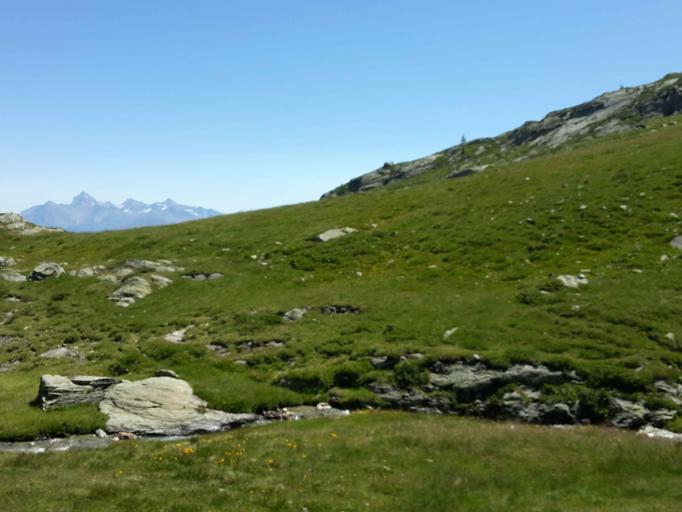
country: IT
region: Aosta Valley
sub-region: Valle d'Aosta
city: Valgrisenche
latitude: 45.6790
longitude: 7.0570
